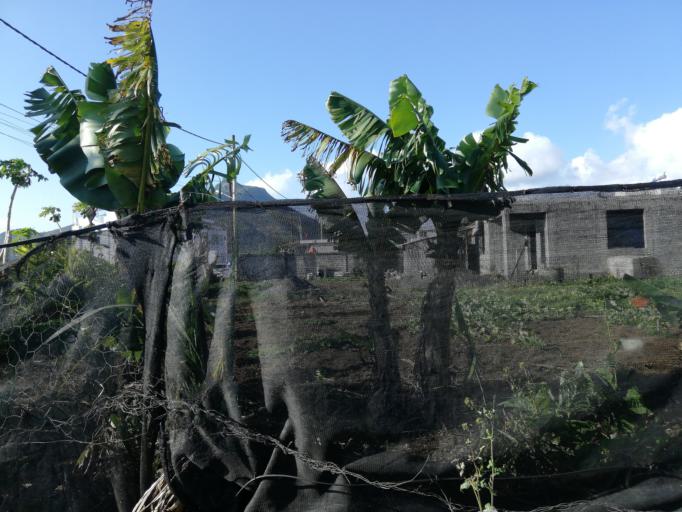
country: MU
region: Moka
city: Saint Pierre
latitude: -20.2191
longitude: 57.5211
